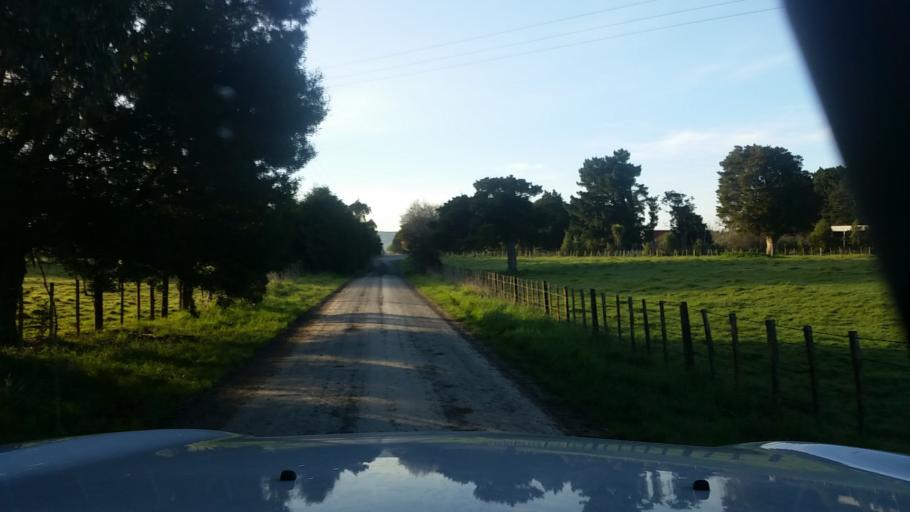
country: NZ
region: Wellington
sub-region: Masterton District
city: Masterton
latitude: -41.0786
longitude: 175.4398
